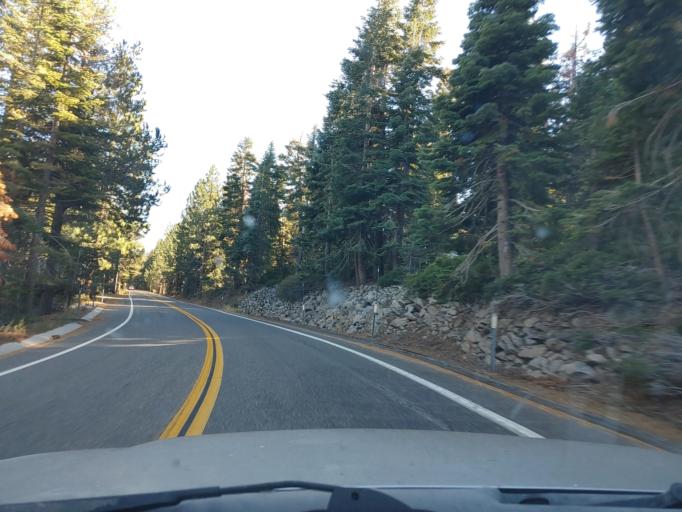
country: US
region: California
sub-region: Placer County
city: Tahoma
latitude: 39.0070
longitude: -120.1173
